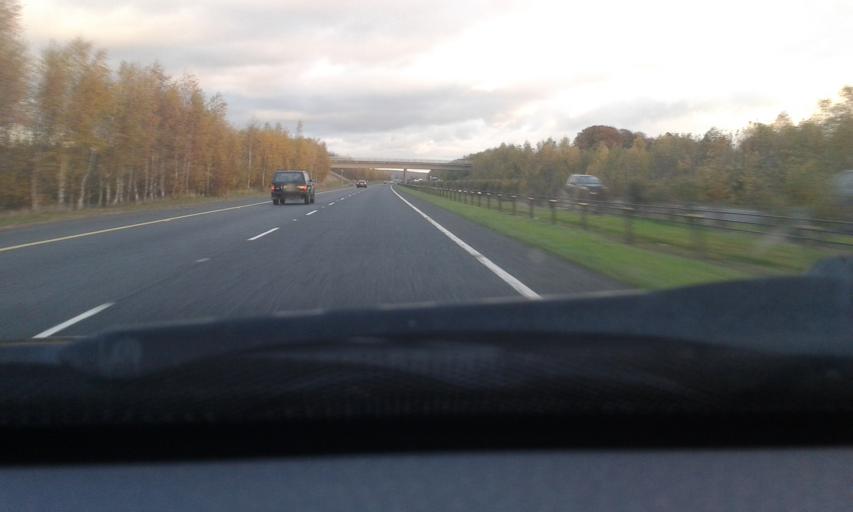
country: IE
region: Leinster
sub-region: Kildare
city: Monasterevin
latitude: 53.1062
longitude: -7.1345
